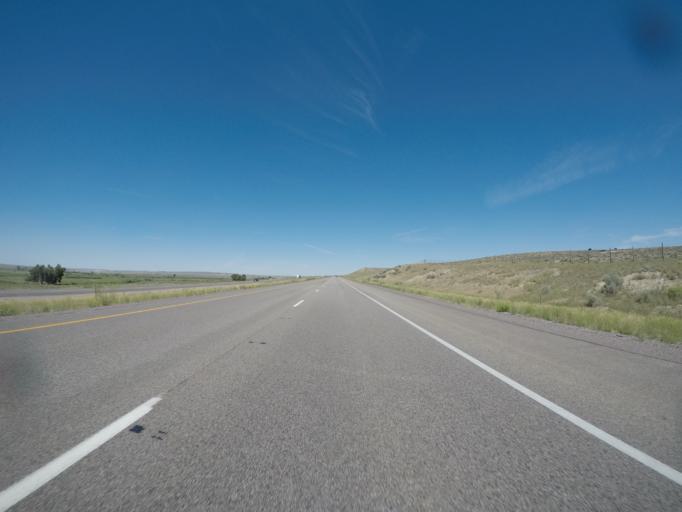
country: US
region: Wyoming
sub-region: Carbon County
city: Saratoga
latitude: 41.7386
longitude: -106.7524
